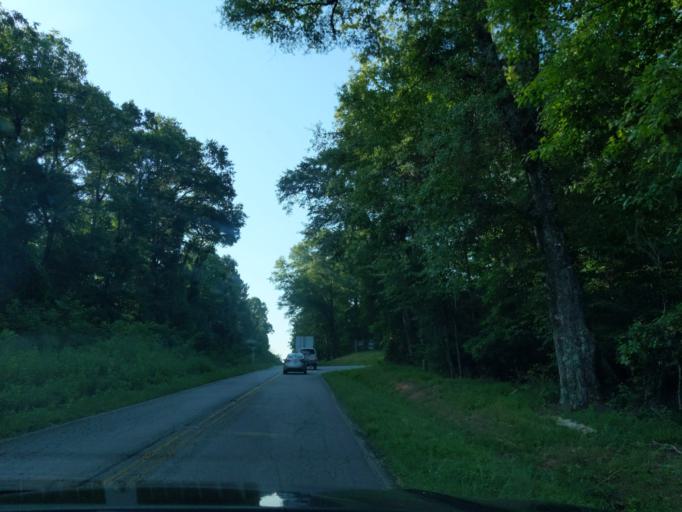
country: US
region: South Carolina
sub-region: Spartanburg County
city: Woodruff
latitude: 34.7776
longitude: -81.9707
